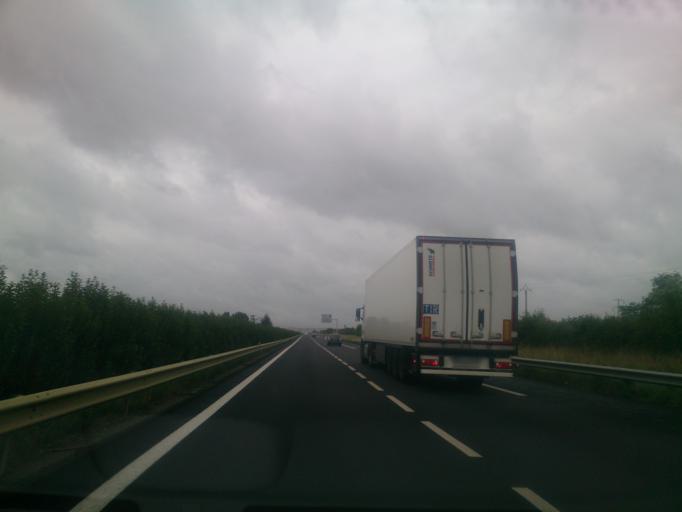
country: FR
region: Midi-Pyrenees
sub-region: Departement de la Haute-Garonne
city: Cazeres
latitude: 43.2408
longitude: 1.0816
